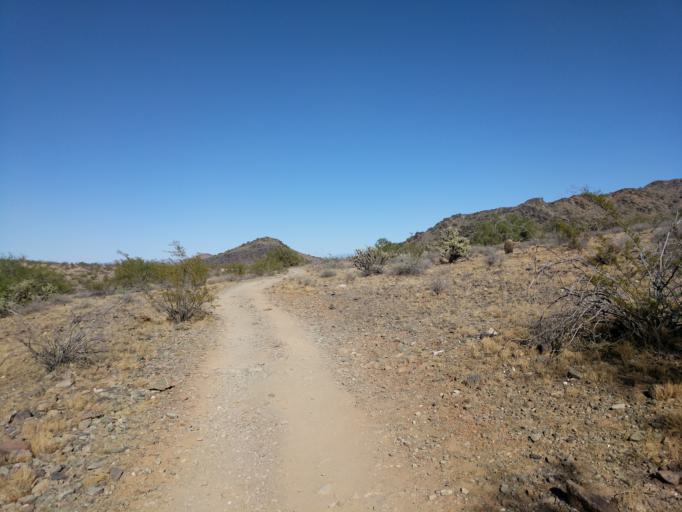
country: US
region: Arizona
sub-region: Maricopa County
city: Glendale
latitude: 33.5923
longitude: -112.0768
